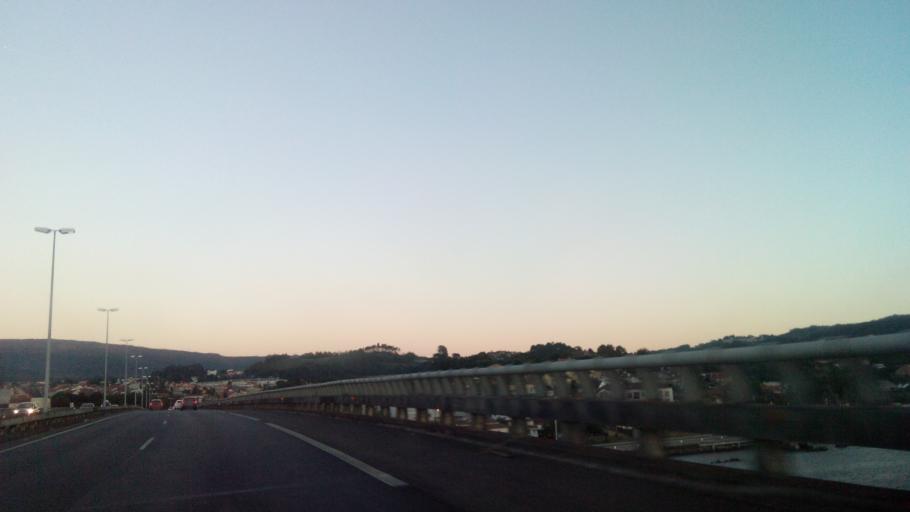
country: ES
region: Galicia
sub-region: Provincia de Pontevedra
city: Poio
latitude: 42.4268
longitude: -8.6551
